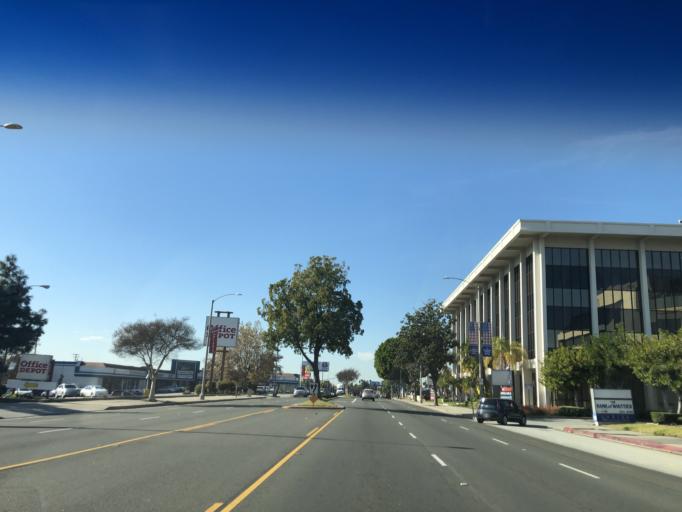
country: US
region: California
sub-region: Los Angeles County
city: East La Mirada
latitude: 33.9481
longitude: -118.0040
